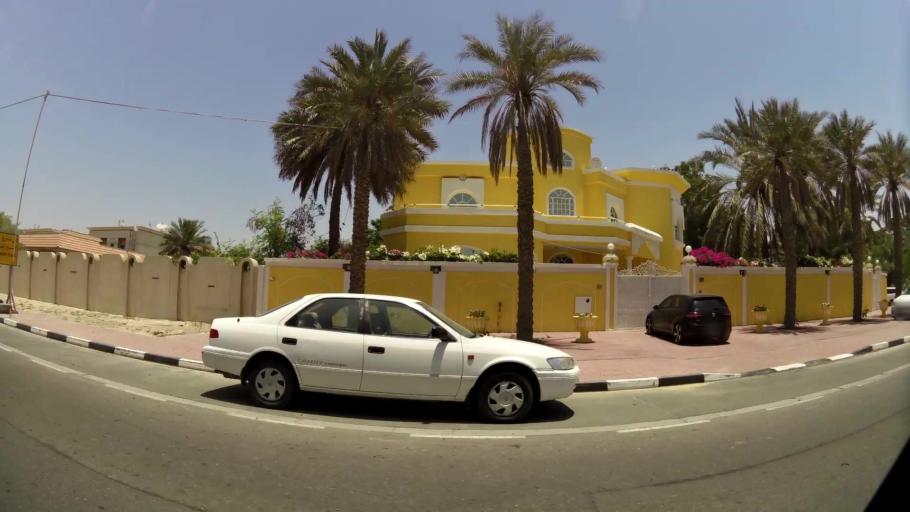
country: AE
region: Ash Shariqah
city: Sharjah
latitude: 25.2389
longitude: 55.2900
